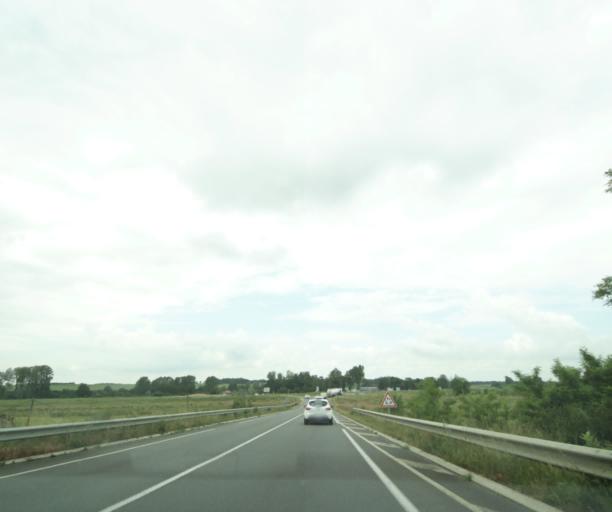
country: FR
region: Poitou-Charentes
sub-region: Departement des Deux-Sevres
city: Sainte-Verge
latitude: 47.0124
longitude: -0.1996
